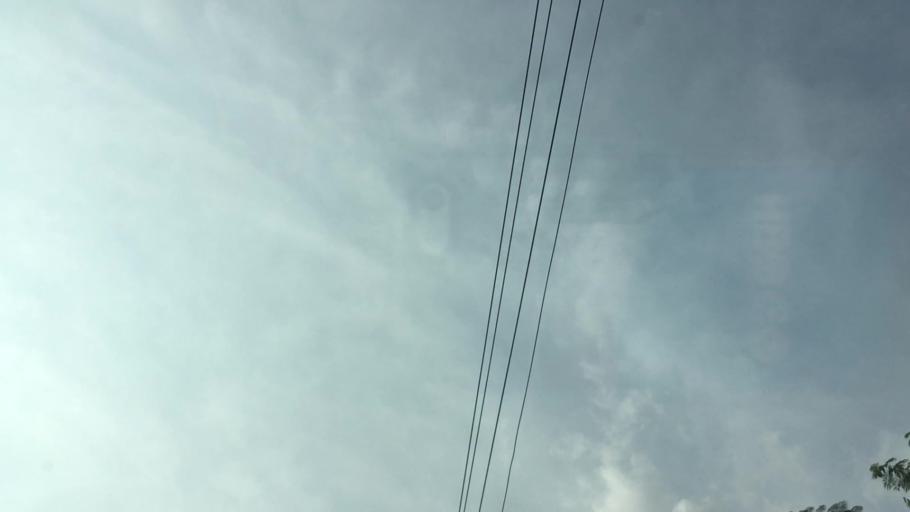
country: US
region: Alabama
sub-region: Bibb County
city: Woodstock
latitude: 33.2194
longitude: -87.1175
